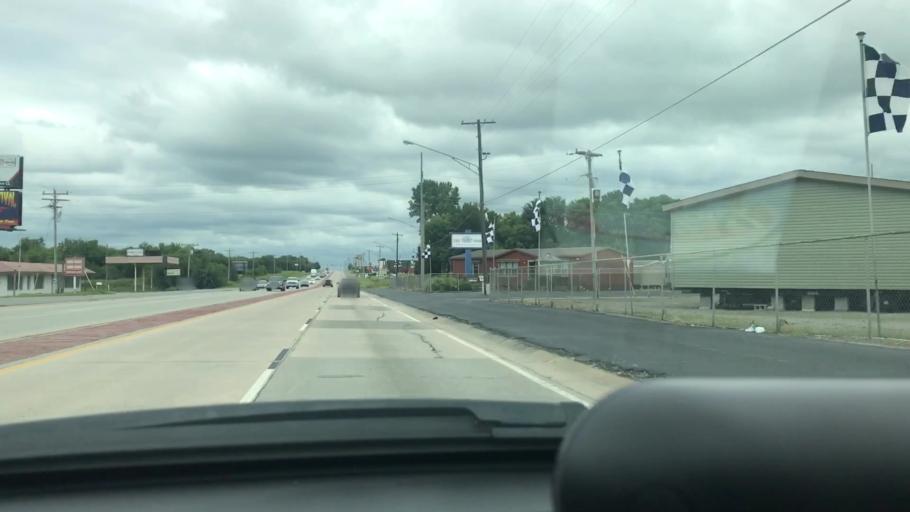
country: US
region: Oklahoma
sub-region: Muskogee County
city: Muskogee
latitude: 35.7755
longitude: -95.4024
